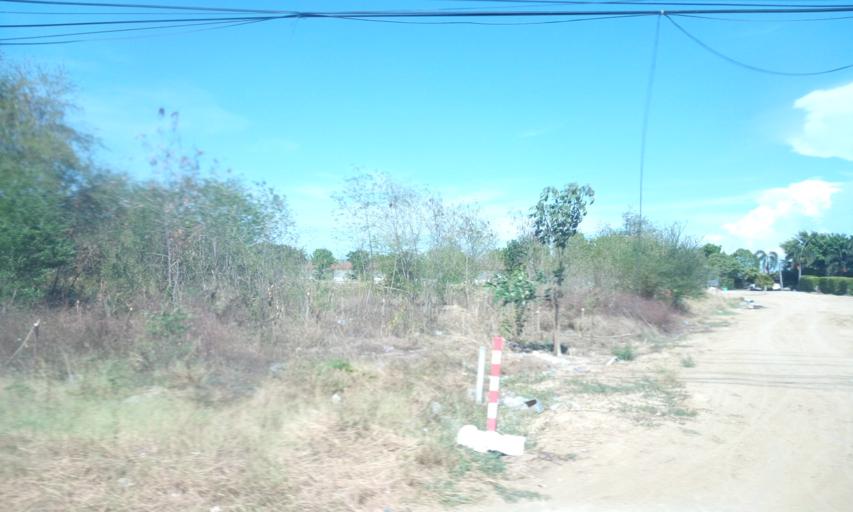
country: TH
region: Samut Prakan
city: Bang Bo District
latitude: 13.5236
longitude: 100.7884
